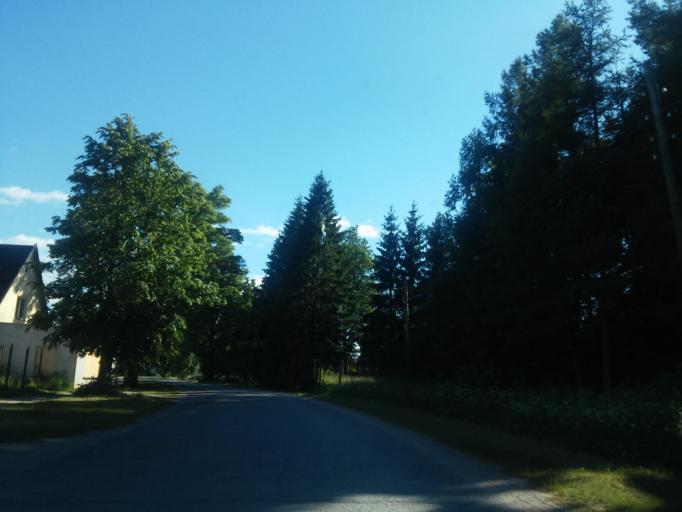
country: LV
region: Vainode
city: Vainode
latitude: 56.4350
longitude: 21.8729
